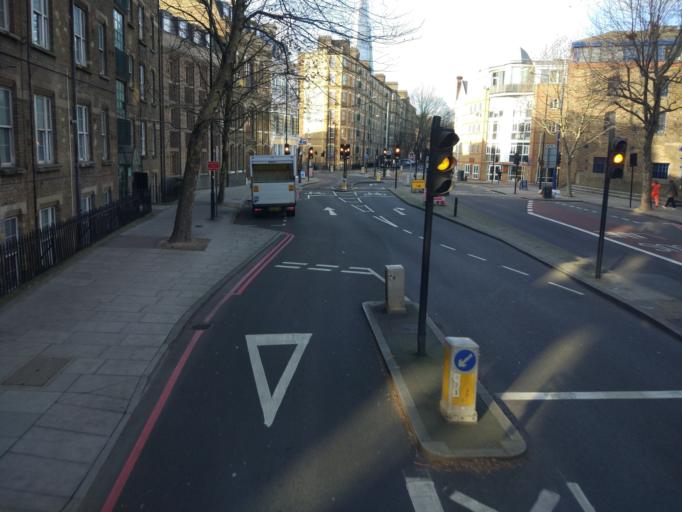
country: GB
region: England
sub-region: Greater London
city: City of London
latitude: 51.5002
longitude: -0.0732
